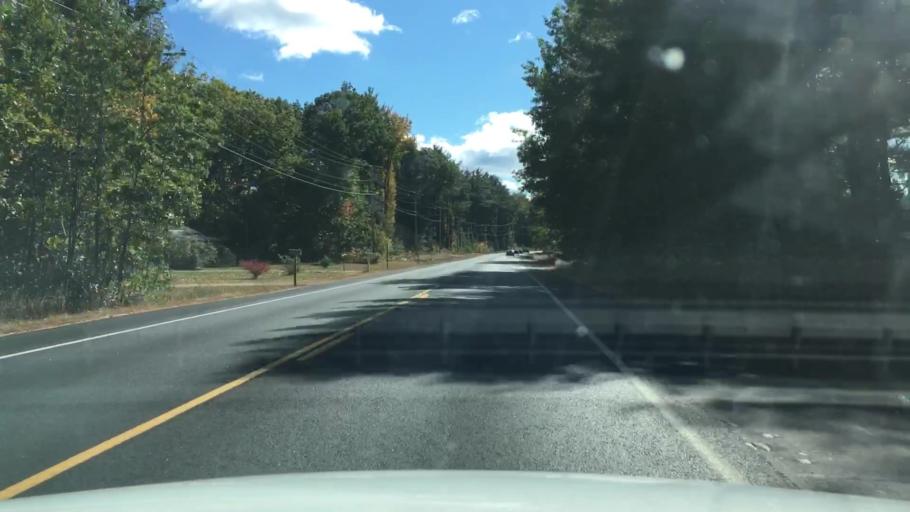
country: US
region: Maine
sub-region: York County
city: South Sanford
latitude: 43.4303
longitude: -70.7333
